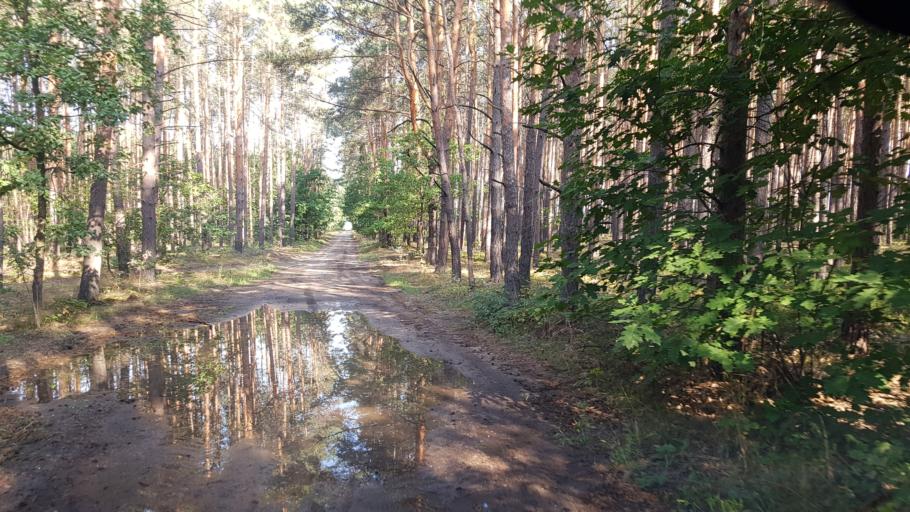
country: DE
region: Brandenburg
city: Finsterwalde
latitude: 51.5961
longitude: 13.6859
